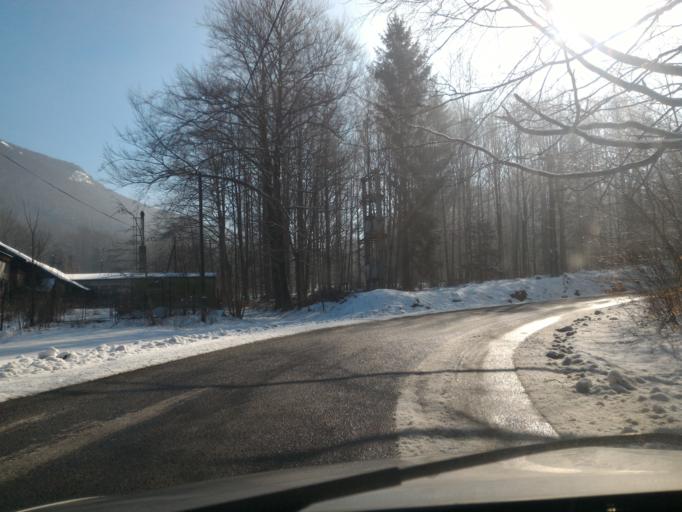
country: CZ
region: Liberecky
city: Nove Mesto pod Smrkem
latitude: 50.8702
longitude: 15.2392
